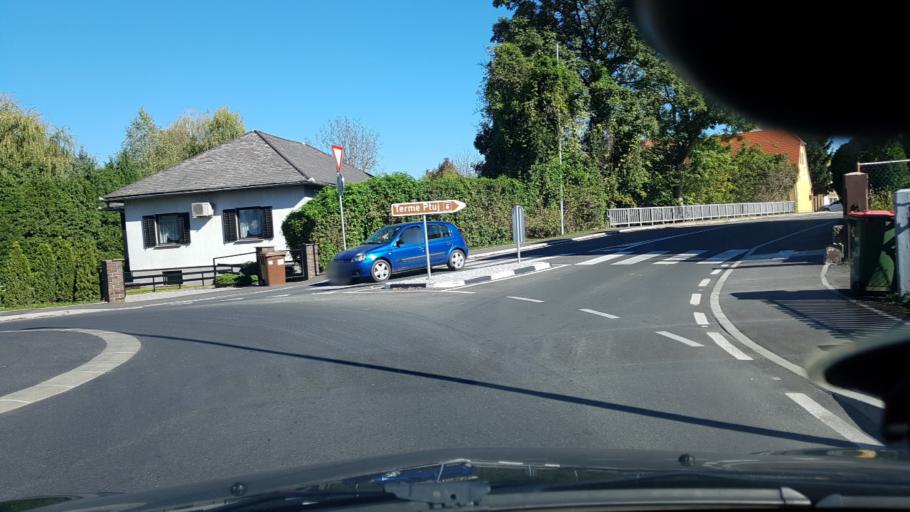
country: SI
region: Ptuj
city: Ptuj
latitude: 46.4155
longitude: 15.8641
